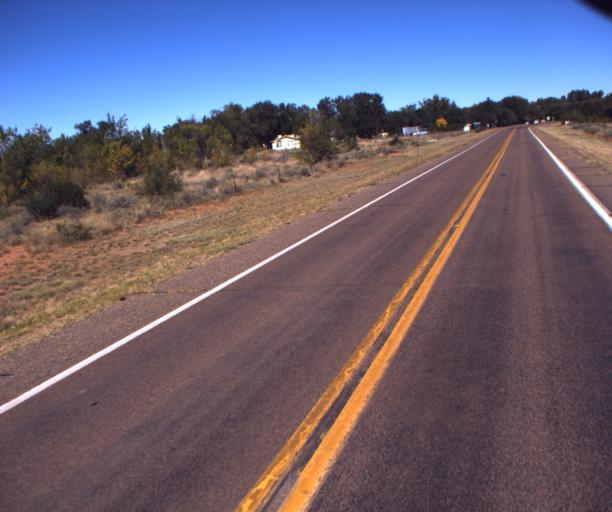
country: US
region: Arizona
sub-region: Apache County
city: Saint Johns
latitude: 34.4942
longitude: -109.3702
